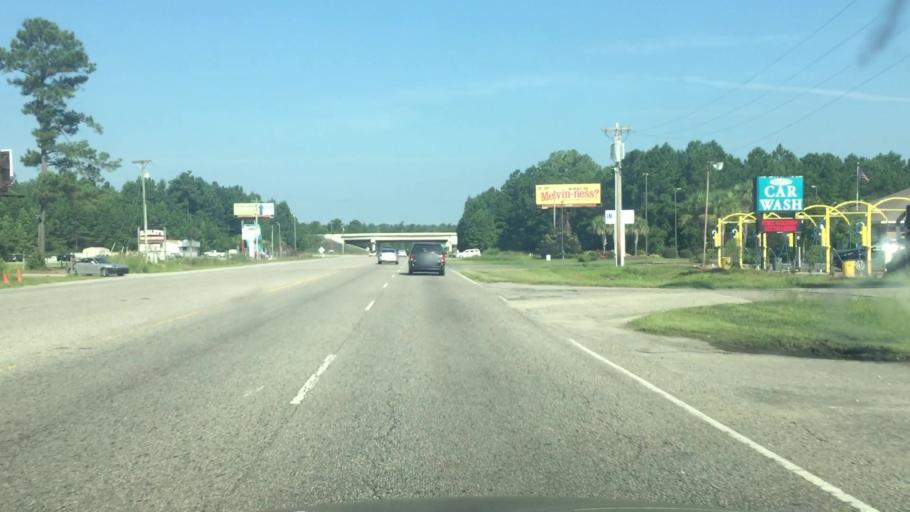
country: US
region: South Carolina
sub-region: Horry County
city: North Myrtle Beach
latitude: 33.8738
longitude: -78.6776
